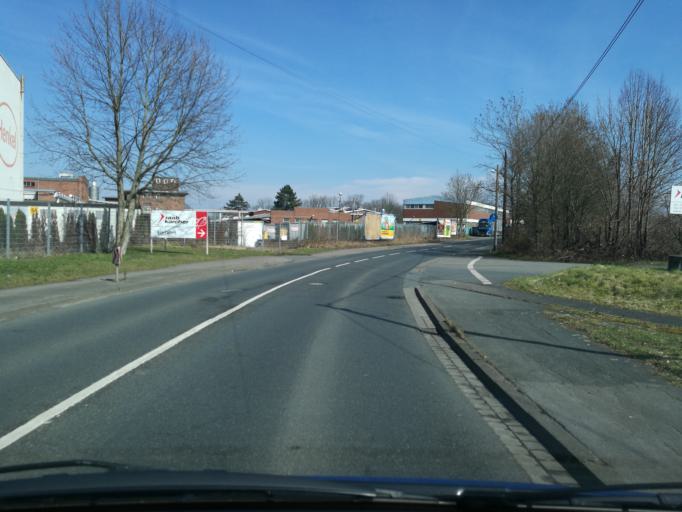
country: DE
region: Lower Saxony
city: Hannover
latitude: 52.3734
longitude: 9.6834
